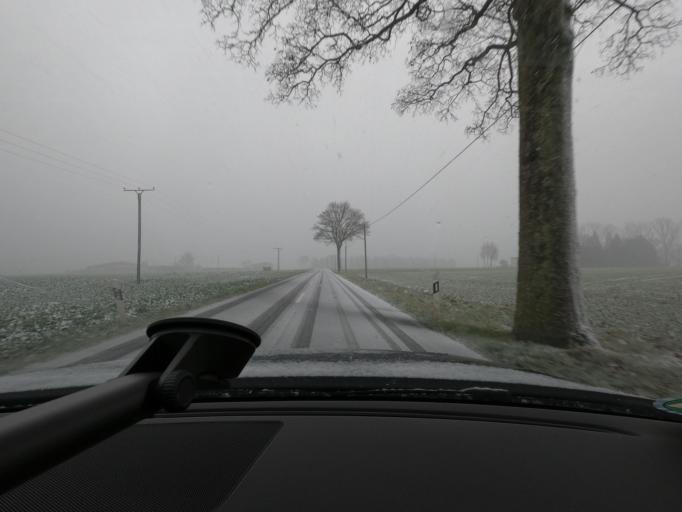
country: DE
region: North Rhine-Westphalia
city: Marsberg
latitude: 51.5274
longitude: 8.8457
